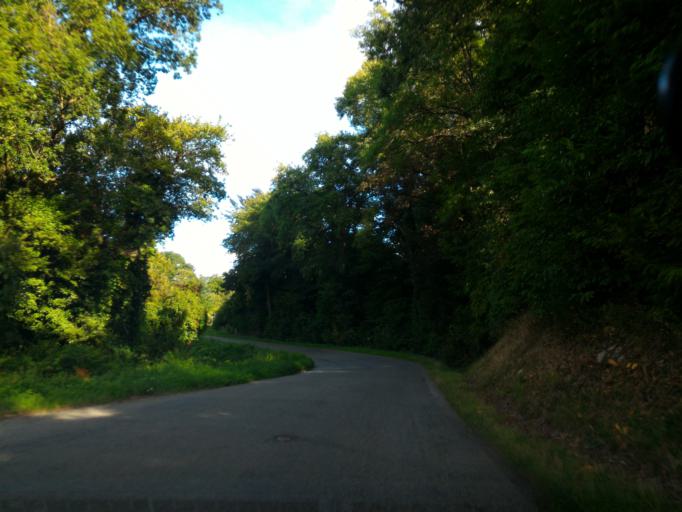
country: FR
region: Poitou-Charentes
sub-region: Departement de la Charente
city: Brigueuil
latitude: 45.9864
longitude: 0.8994
